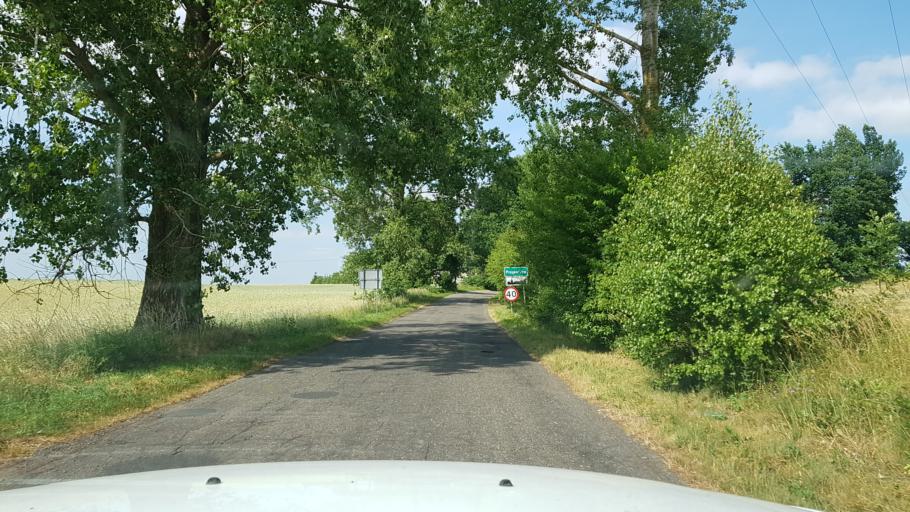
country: PL
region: West Pomeranian Voivodeship
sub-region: Powiat goleniowski
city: Mosty
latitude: 53.5726
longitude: 14.9759
